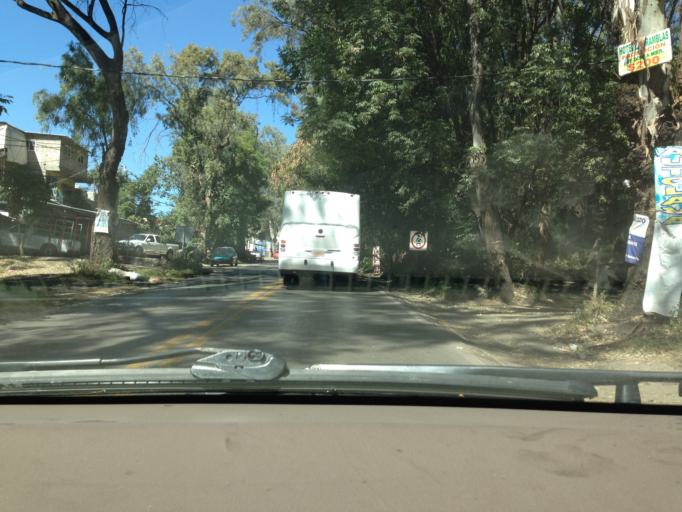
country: MX
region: Morelos
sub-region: Cuernavaca
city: Fraccionamiento Lomas de Ahuatlan
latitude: 18.9706
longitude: -99.2492
